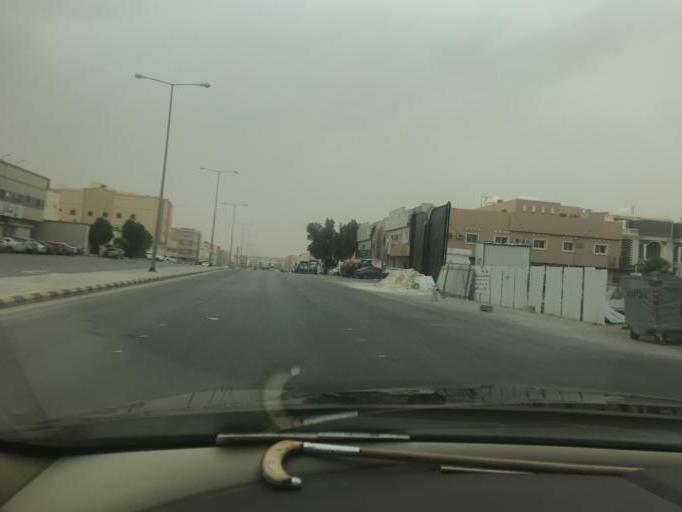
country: SA
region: Ar Riyad
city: Riyadh
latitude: 24.7849
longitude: 46.6948
